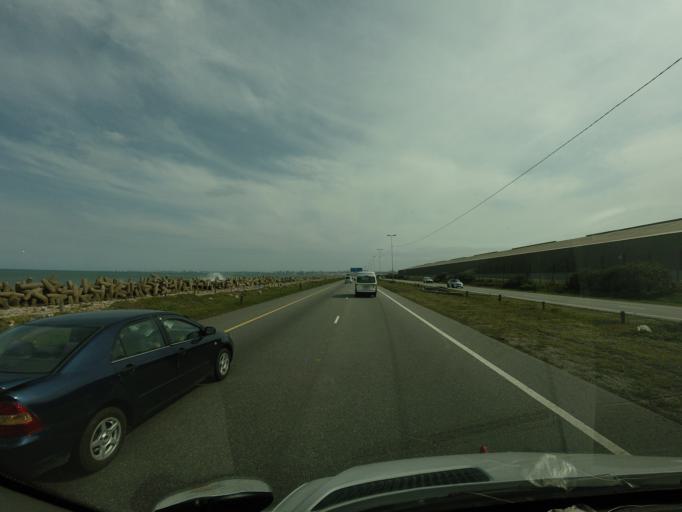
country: ZA
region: Eastern Cape
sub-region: Nelson Mandela Bay Metropolitan Municipality
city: Port Elizabeth
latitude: -33.9040
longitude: 25.6184
